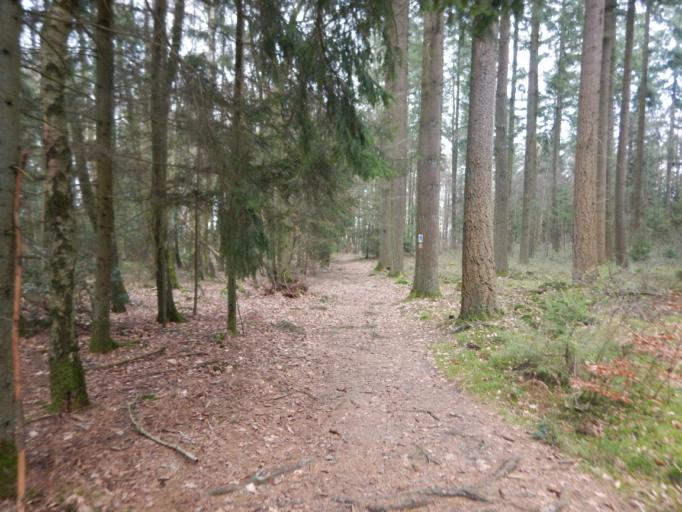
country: LU
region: Grevenmacher
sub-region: Canton d'Echternach
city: Beaufort
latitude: 49.8458
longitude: 6.3078
